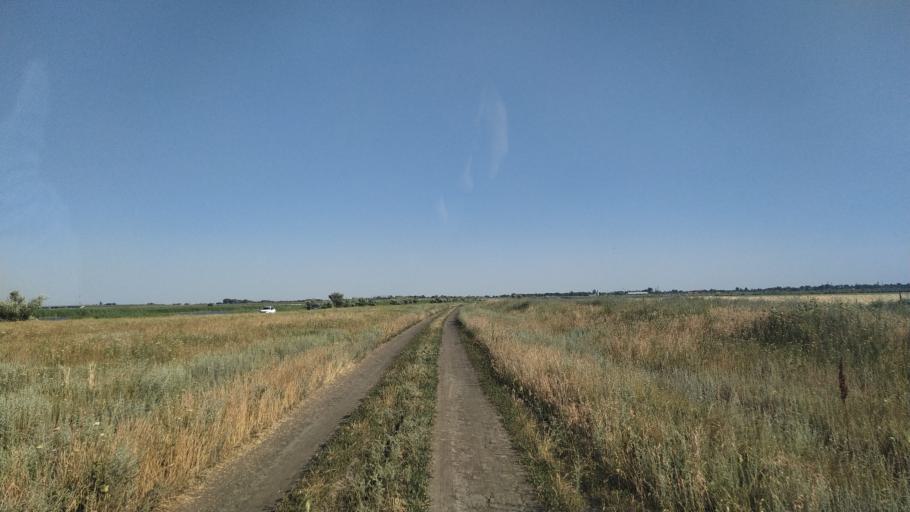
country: RU
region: Rostov
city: Kuleshovka
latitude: 47.1279
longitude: 39.6452
